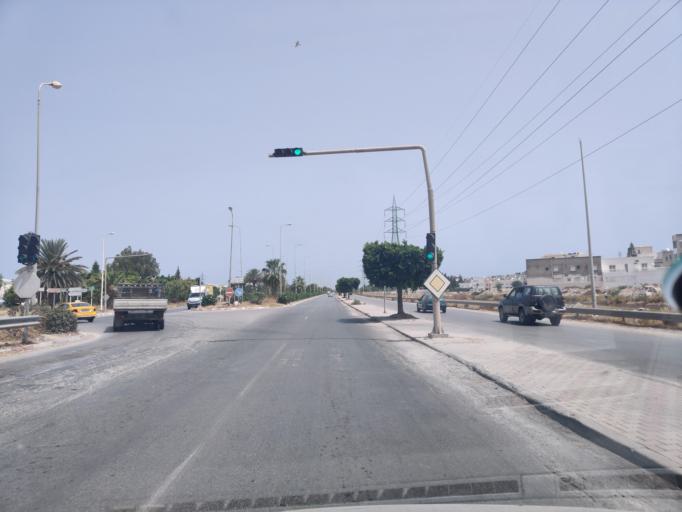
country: TN
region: Tunis
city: Carthage
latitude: 36.8511
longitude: 10.3061
